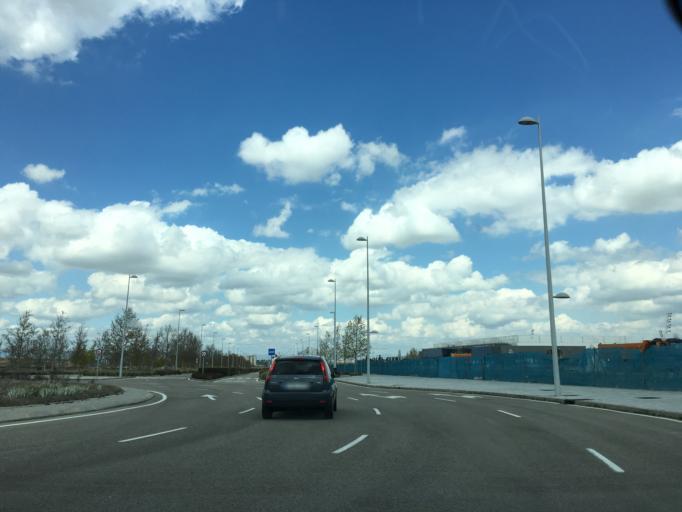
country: ES
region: Madrid
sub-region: Provincia de Madrid
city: Hortaleza
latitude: 40.4760
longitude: -3.6179
